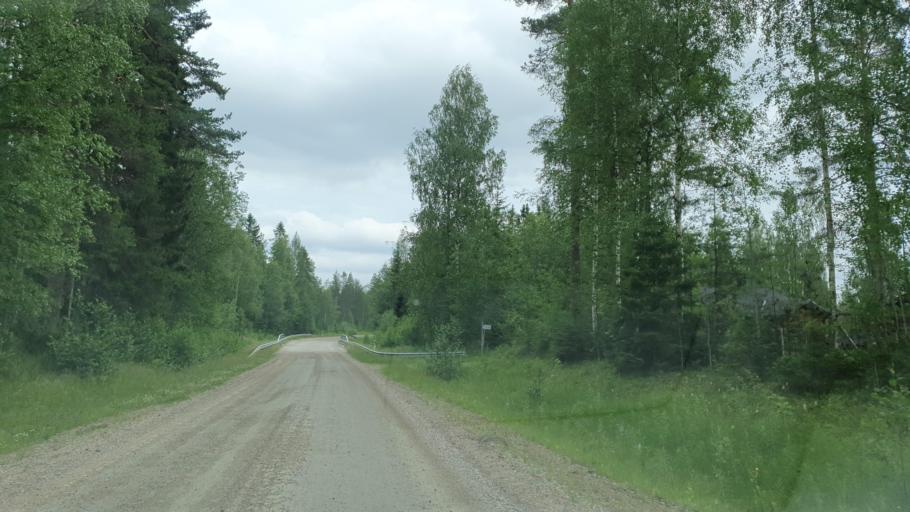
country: FI
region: Kainuu
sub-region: Kehys-Kainuu
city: Kuhmo
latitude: 63.9725
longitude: 29.3159
